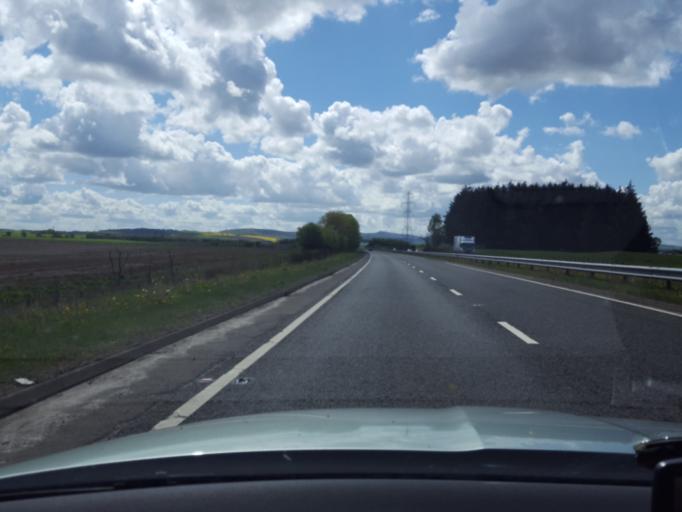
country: GB
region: Scotland
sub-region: Angus
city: Forfar
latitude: 56.6616
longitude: -2.9134
